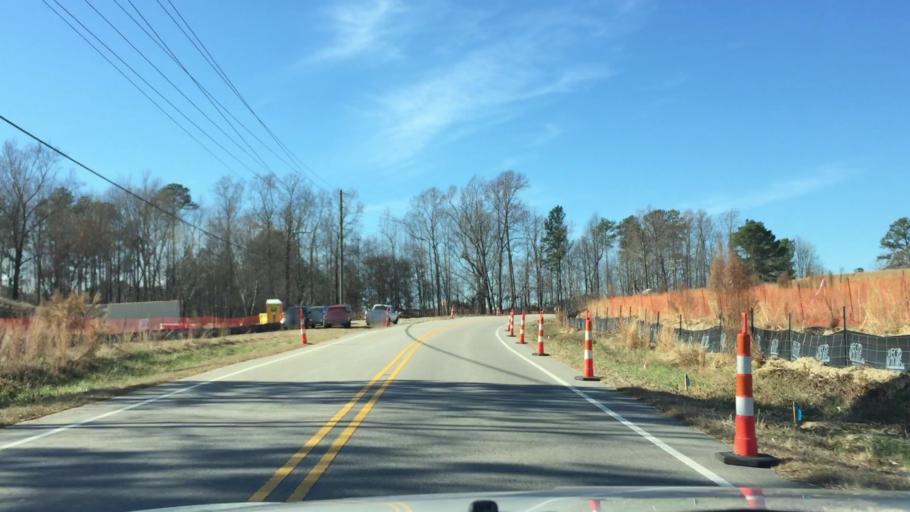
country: US
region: North Carolina
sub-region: Wake County
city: Apex
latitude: 35.7587
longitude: -78.8714
